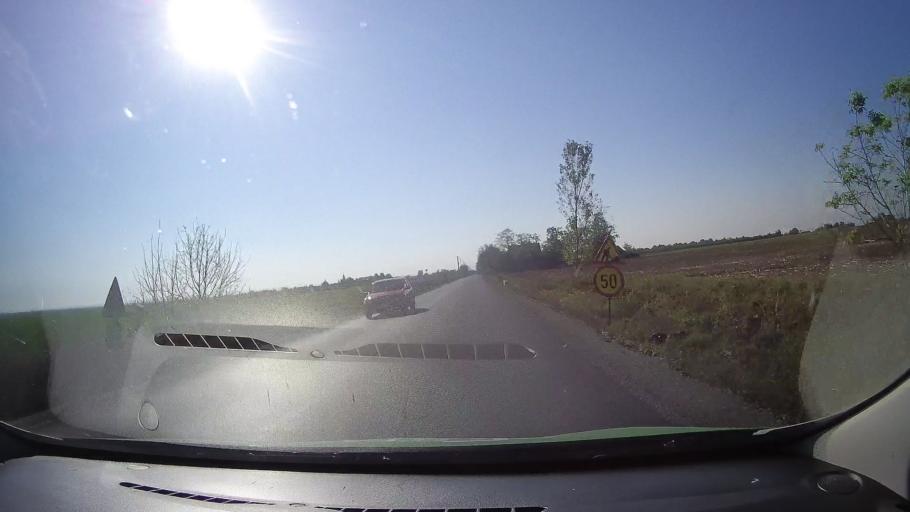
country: RO
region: Satu Mare
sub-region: Comuna Tiream
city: Tiream
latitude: 47.6237
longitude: 22.4679
